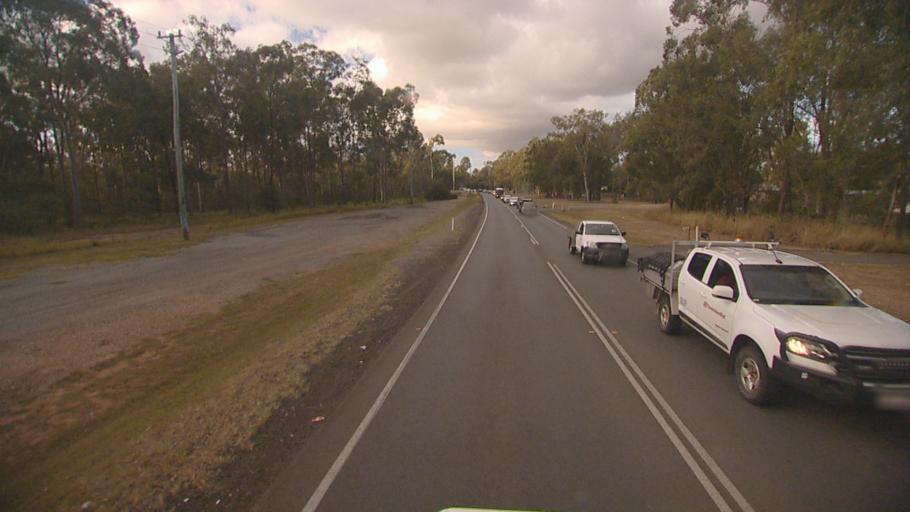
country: AU
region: Queensland
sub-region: Logan
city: Park Ridge South
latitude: -27.7176
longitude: 152.9908
